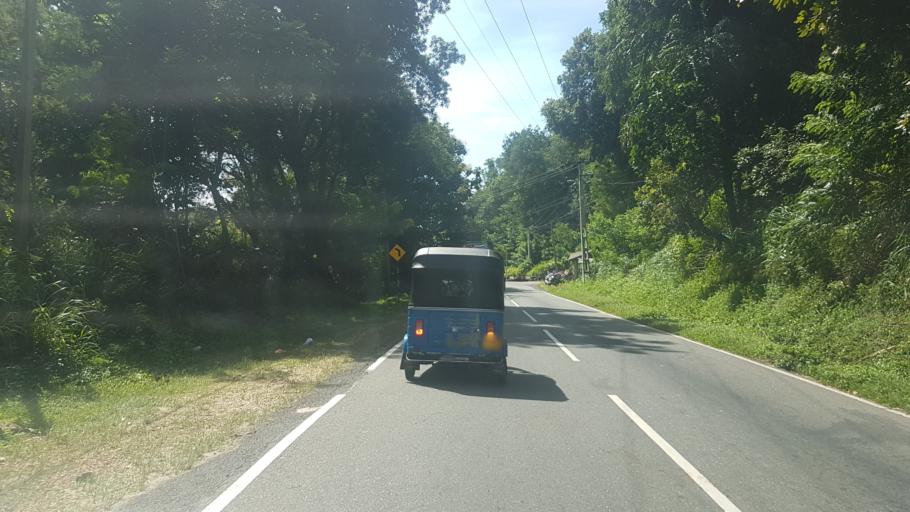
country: LK
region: Uva
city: Haputale
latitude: 6.8062
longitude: 81.0846
